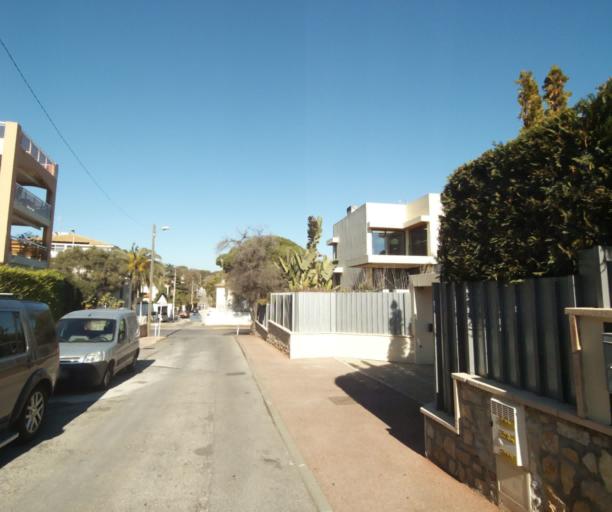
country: FR
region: Provence-Alpes-Cote d'Azur
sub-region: Departement des Alpes-Maritimes
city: Antibes
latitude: 43.5691
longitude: 7.1219
